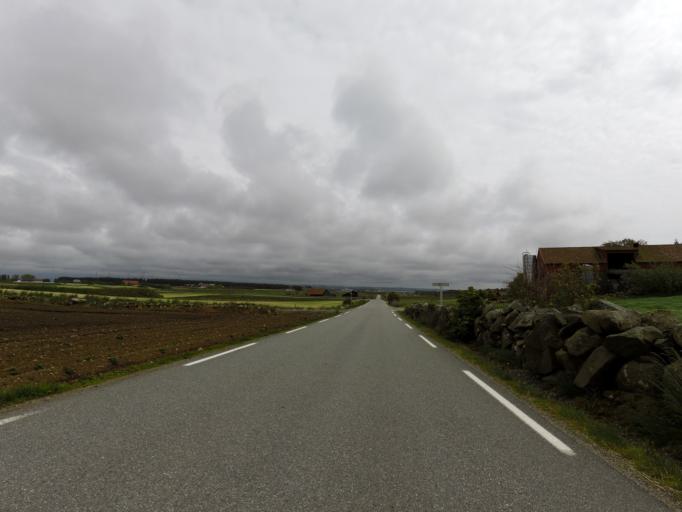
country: NO
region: Rogaland
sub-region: Ha
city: Naerbo
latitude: 58.6546
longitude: 5.5768
